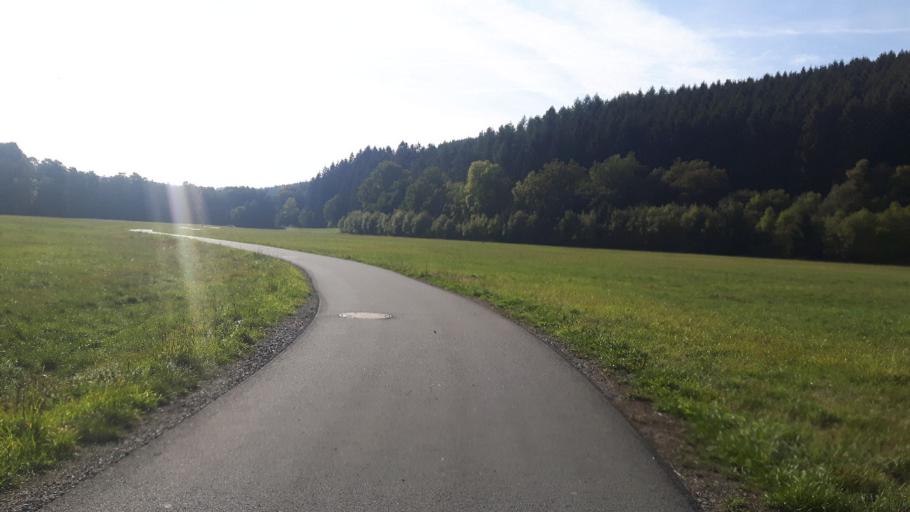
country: DE
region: North Rhine-Westphalia
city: Netphen
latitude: 50.9053
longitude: 8.1131
